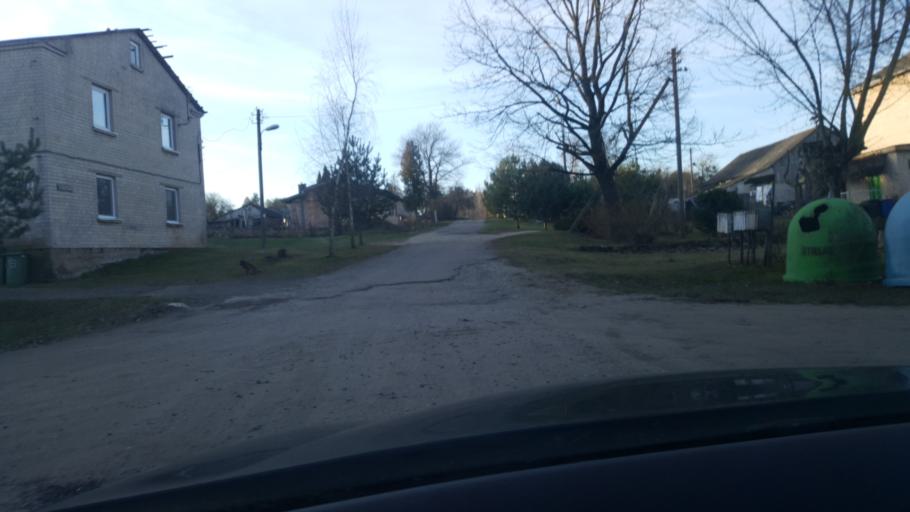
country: LT
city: Prienai
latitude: 54.7126
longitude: 23.9571
